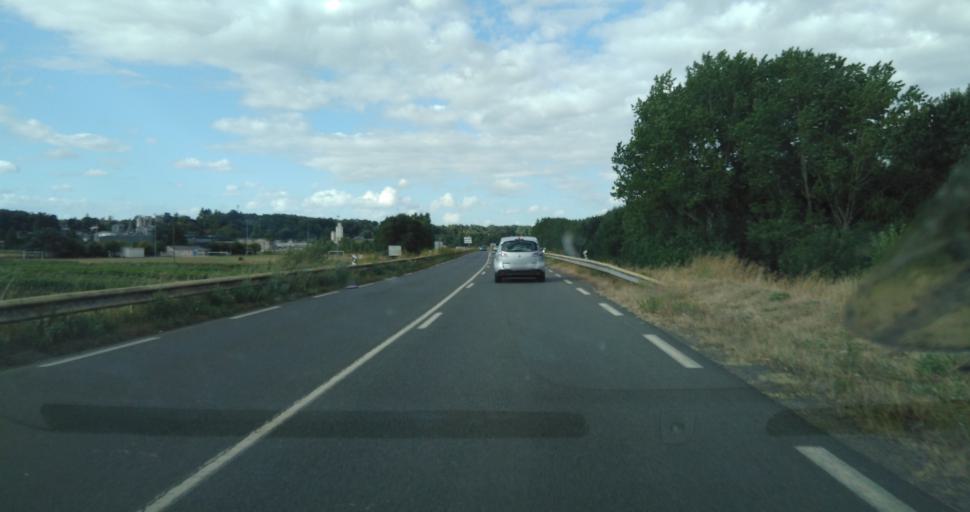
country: FR
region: Centre
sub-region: Departement d'Indre-et-Loire
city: Cinq-Mars-la-Pile
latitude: 47.3372
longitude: 0.4630
